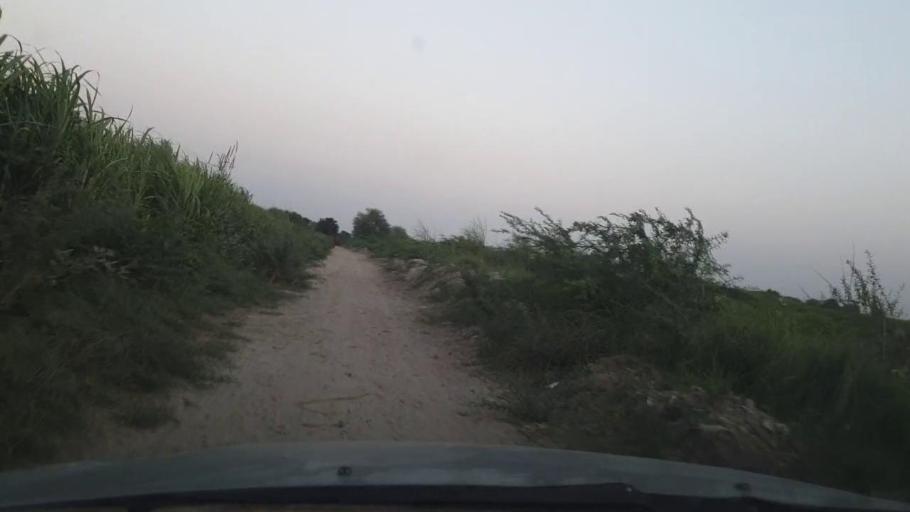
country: PK
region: Sindh
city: Digri
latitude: 25.1162
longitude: 68.9997
